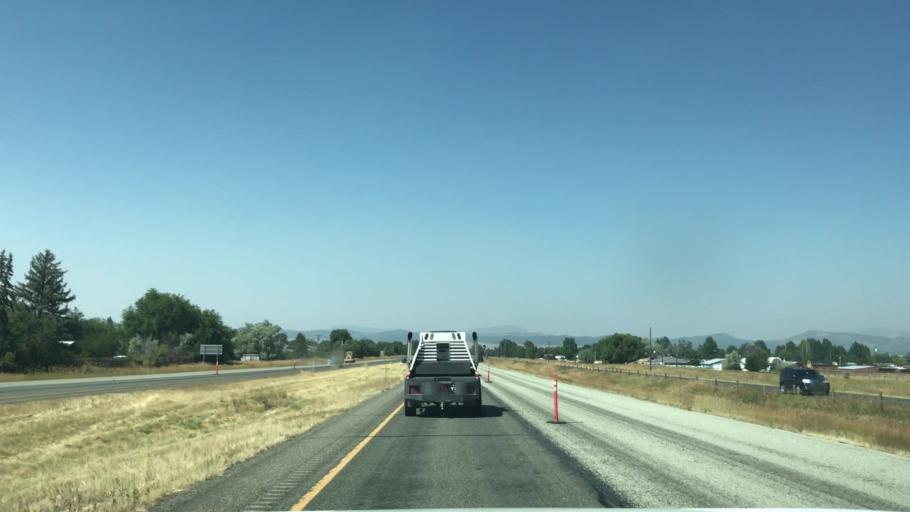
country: US
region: Montana
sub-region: Lewis and Clark County
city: Helena
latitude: 46.6363
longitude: -112.0111
